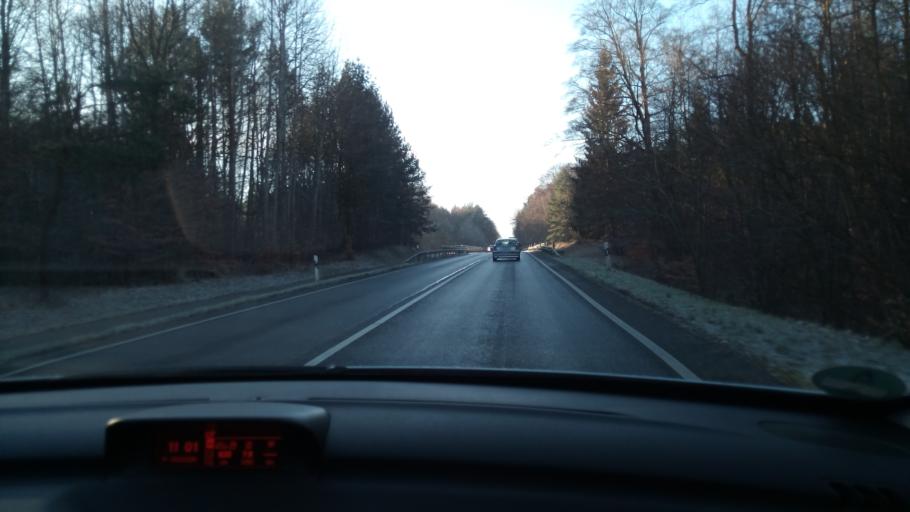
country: DE
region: Mecklenburg-Vorpommern
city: Neustrelitz
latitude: 53.3881
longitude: 13.0921
